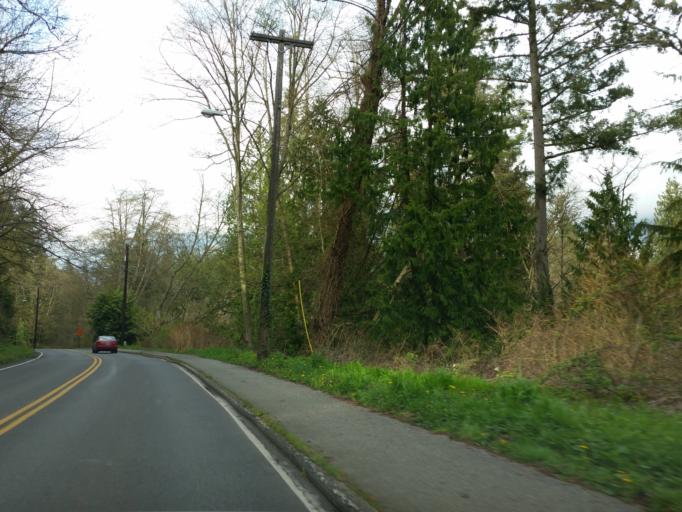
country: US
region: Washington
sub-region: Snohomish County
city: Meadowdale
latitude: 47.8337
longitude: -122.3391
